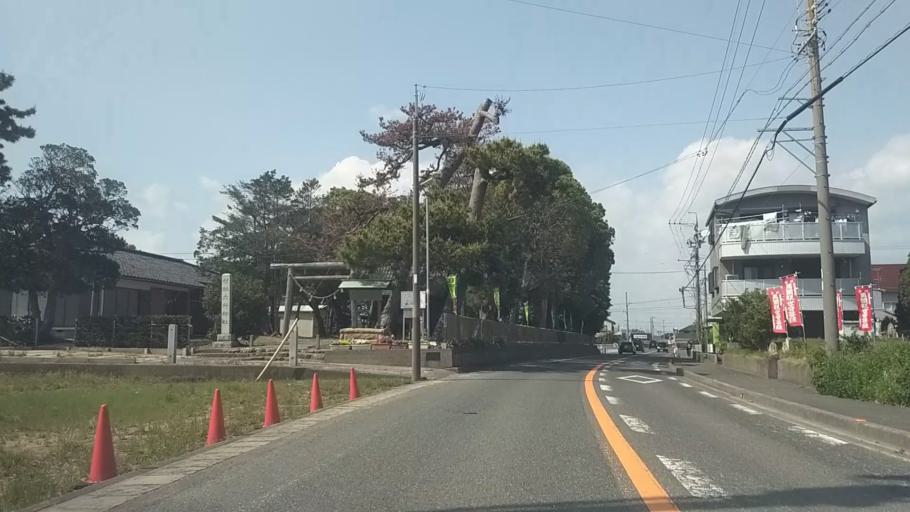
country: JP
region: Shizuoka
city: Hamamatsu
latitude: 34.6771
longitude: 137.7077
